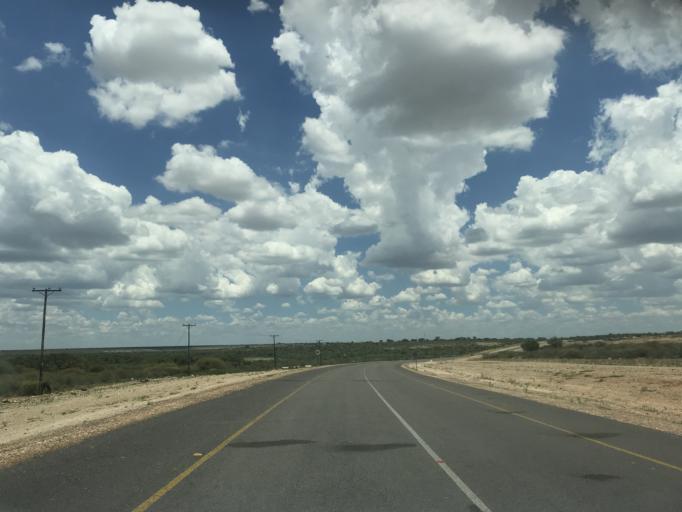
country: BW
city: Mabuli
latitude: -25.7802
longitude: 24.9160
